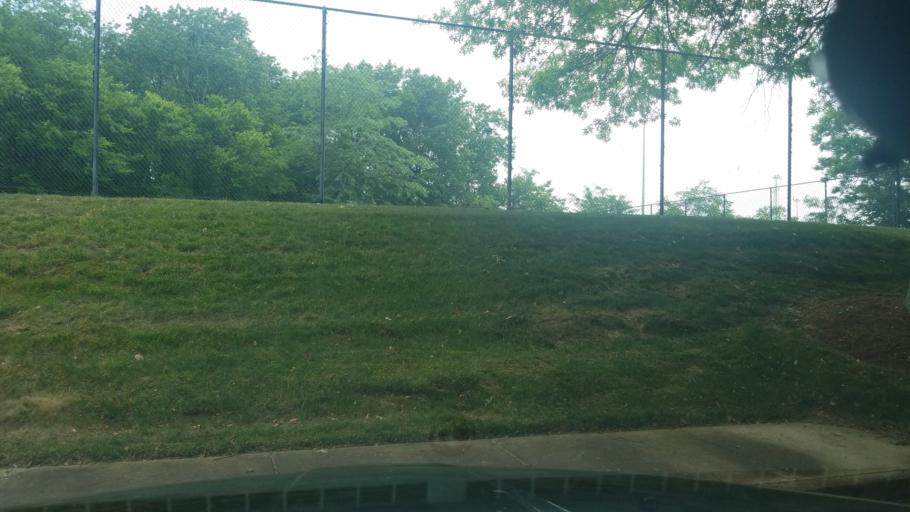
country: US
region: Tennessee
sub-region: Davidson County
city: Goodlettsville
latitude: 36.2668
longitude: -86.7402
